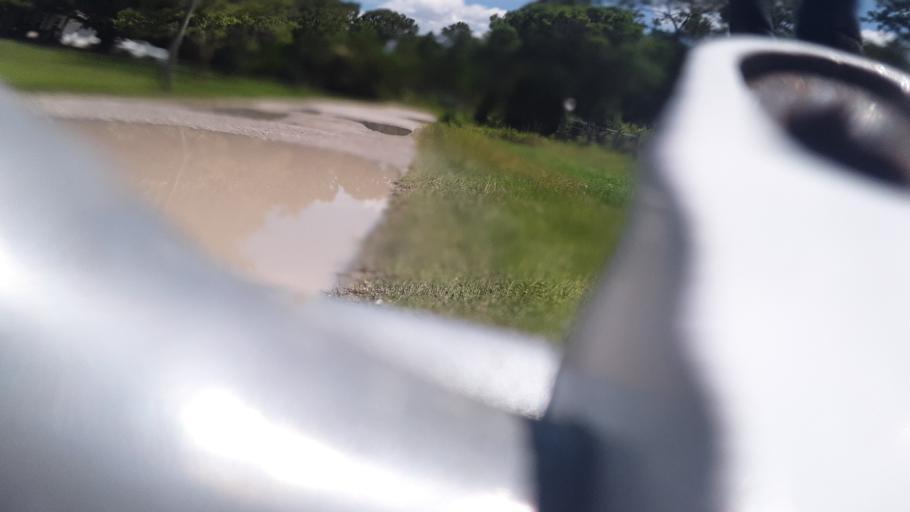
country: US
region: Florida
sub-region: Brevard County
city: Malabar
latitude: 27.9890
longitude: -80.6100
